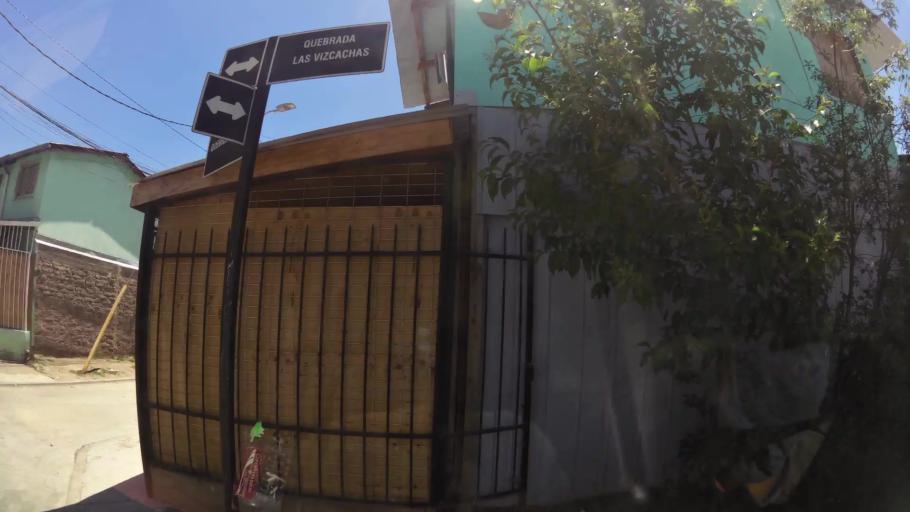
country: CL
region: Santiago Metropolitan
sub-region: Provincia de Maipo
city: San Bernardo
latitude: -33.5979
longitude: -70.6746
